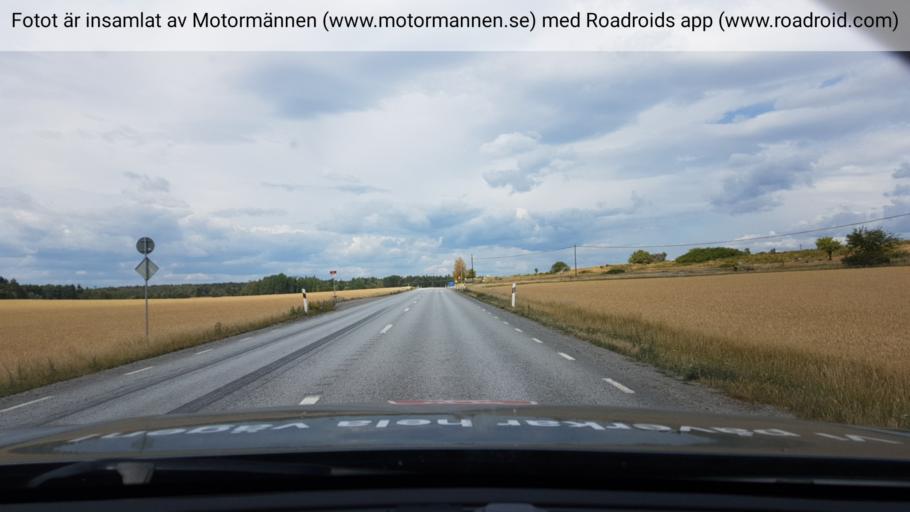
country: SE
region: Uppsala
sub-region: Habo Kommun
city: Balsta
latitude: 59.6239
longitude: 17.6047
